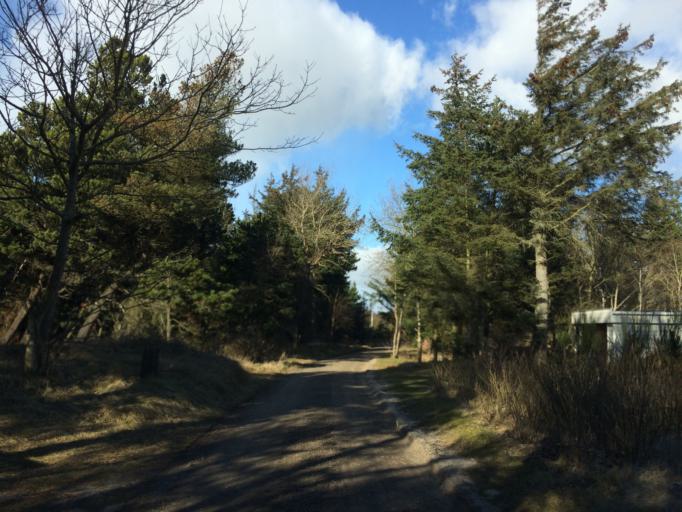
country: DK
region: Central Jutland
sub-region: Holstebro Kommune
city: Ulfborg
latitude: 56.2610
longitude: 8.1434
